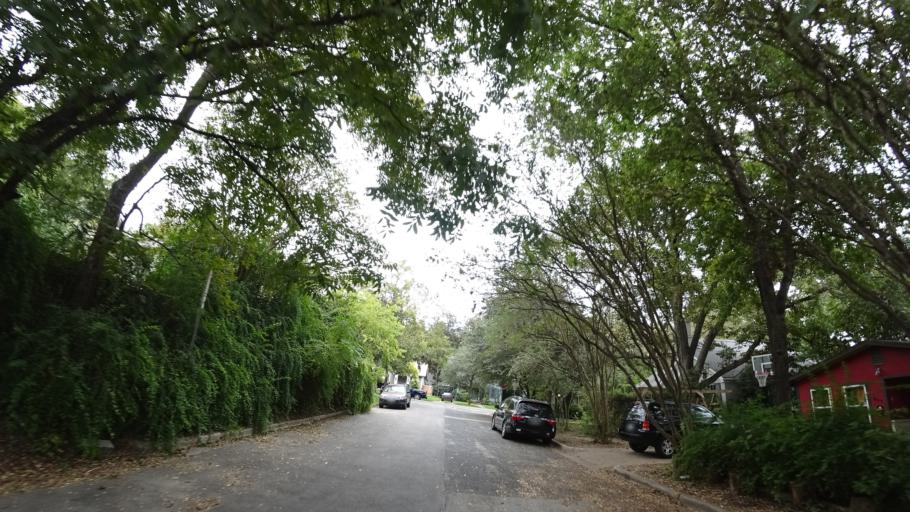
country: US
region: Texas
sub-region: Travis County
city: Austin
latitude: 30.2924
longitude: -97.7282
